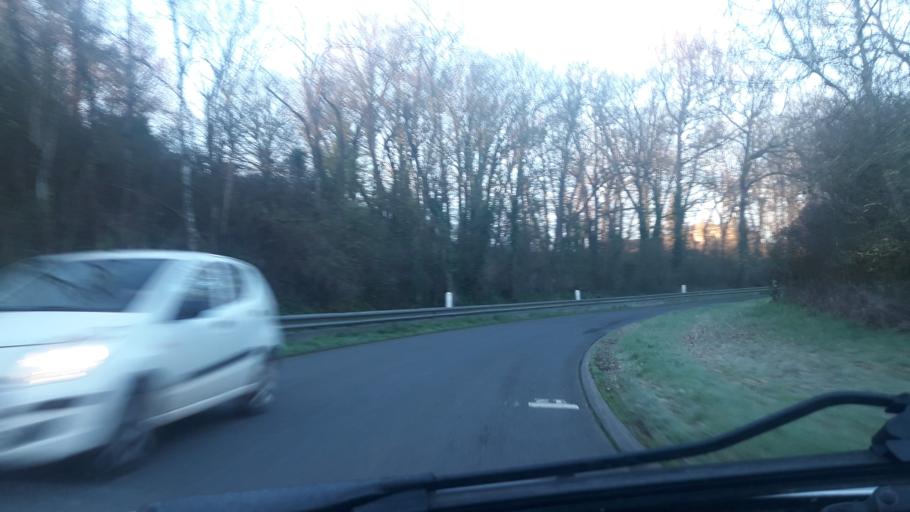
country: FR
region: Midi-Pyrenees
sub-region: Departement de la Haute-Garonne
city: Berat
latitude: 43.4190
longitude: 1.1766
